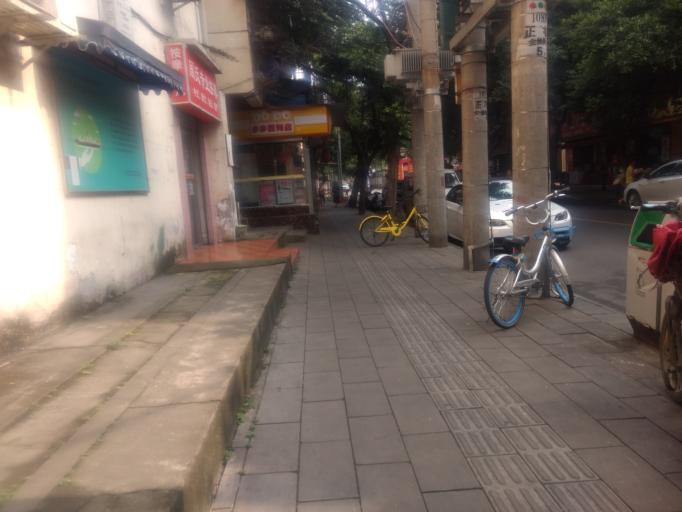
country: CN
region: Sichuan
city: Chengdu
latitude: 30.6745
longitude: 104.0688
